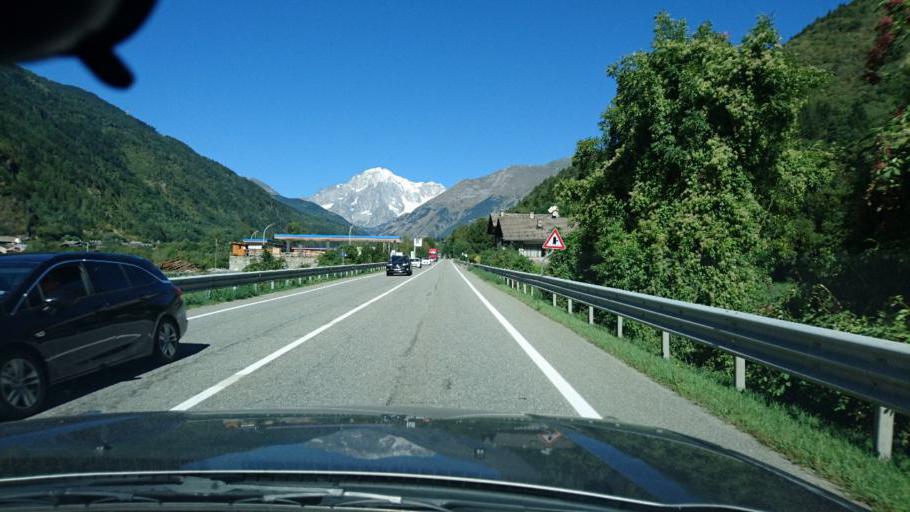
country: IT
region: Aosta Valley
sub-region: Valle d'Aosta
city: La Salle
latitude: 45.7236
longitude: 7.0979
